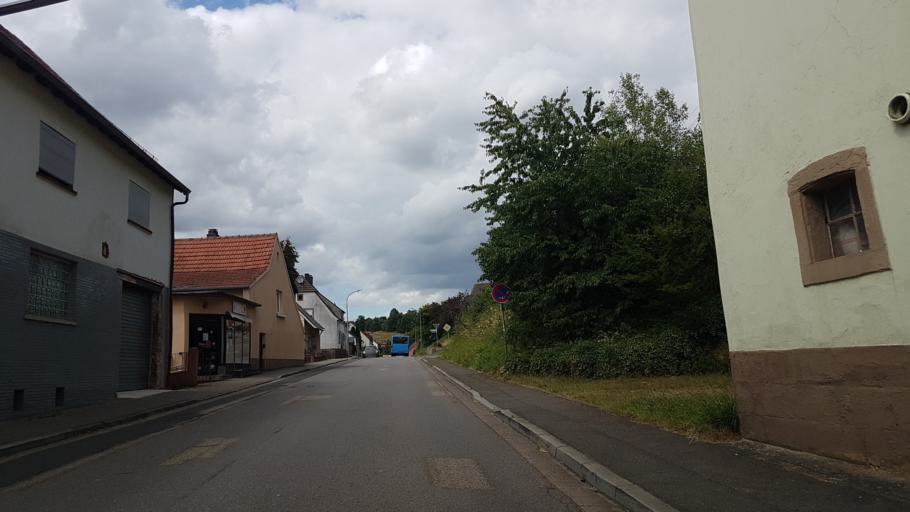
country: DE
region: Rheinland-Pfalz
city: Altenkirchen
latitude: 49.4433
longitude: 7.3226
